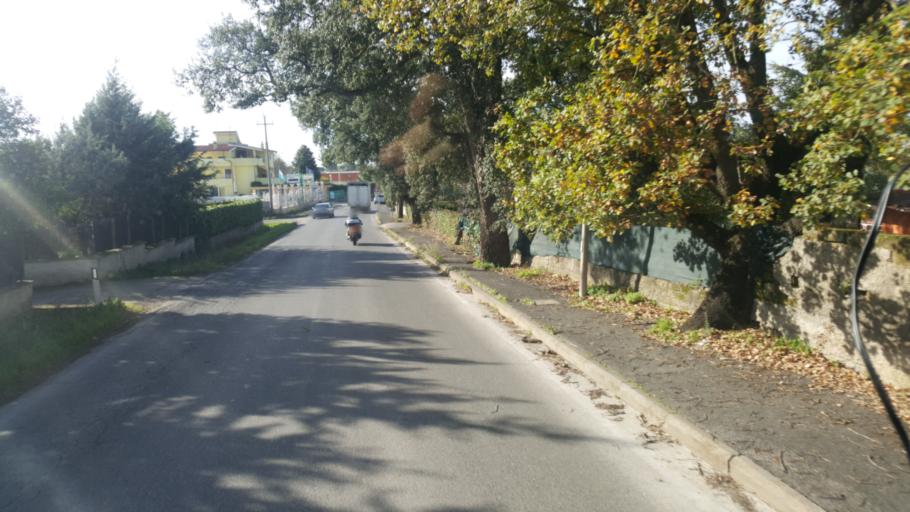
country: IT
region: Latium
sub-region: Provincia di Latina
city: Casalazzara
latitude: 41.6286
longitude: 12.5971
